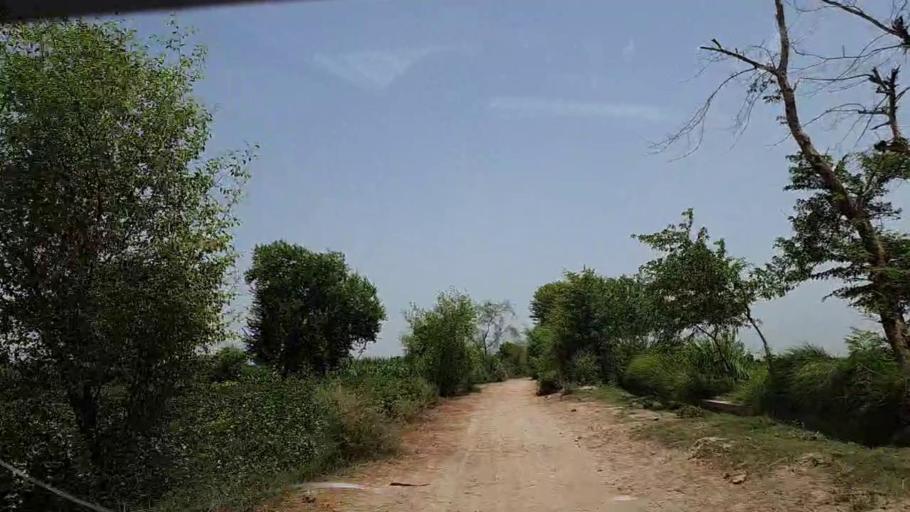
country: PK
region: Sindh
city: Tharu Shah
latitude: 26.9349
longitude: 68.0336
